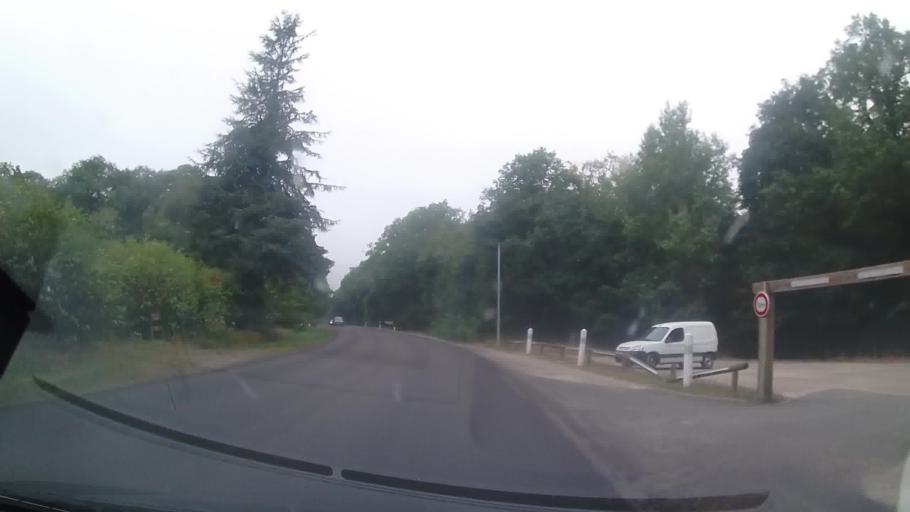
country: FR
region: Ile-de-France
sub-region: Departement de l'Essonne
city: Dourdan
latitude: 48.5426
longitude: 1.9967
